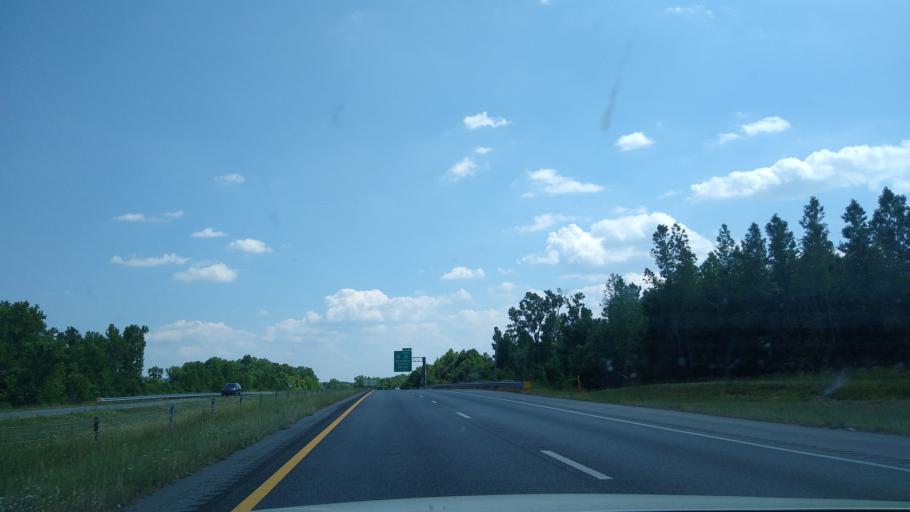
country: US
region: North Carolina
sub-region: Guilford County
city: McLeansville
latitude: 36.0730
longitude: -79.6921
